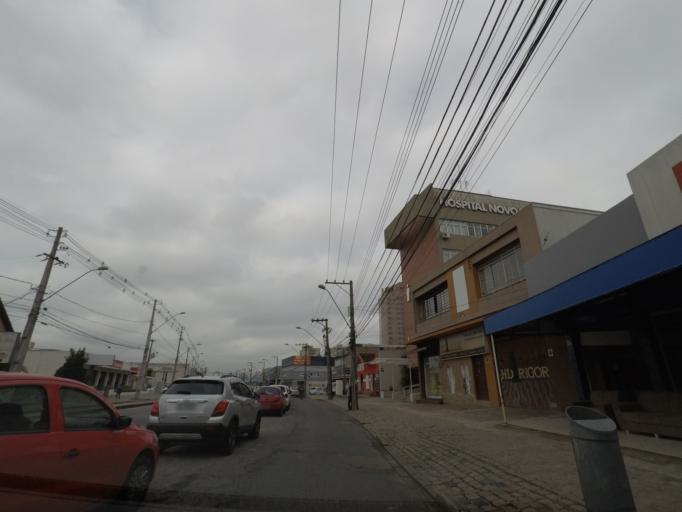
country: BR
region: Parana
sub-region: Curitiba
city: Curitiba
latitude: -25.4866
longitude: -49.2944
